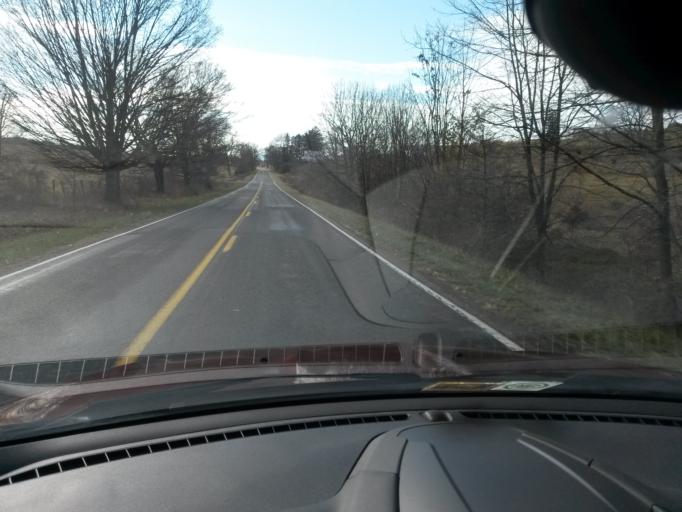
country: US
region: Virginia
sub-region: Rockingham County
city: Bridgewater
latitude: 38.3240
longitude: -79.0630
